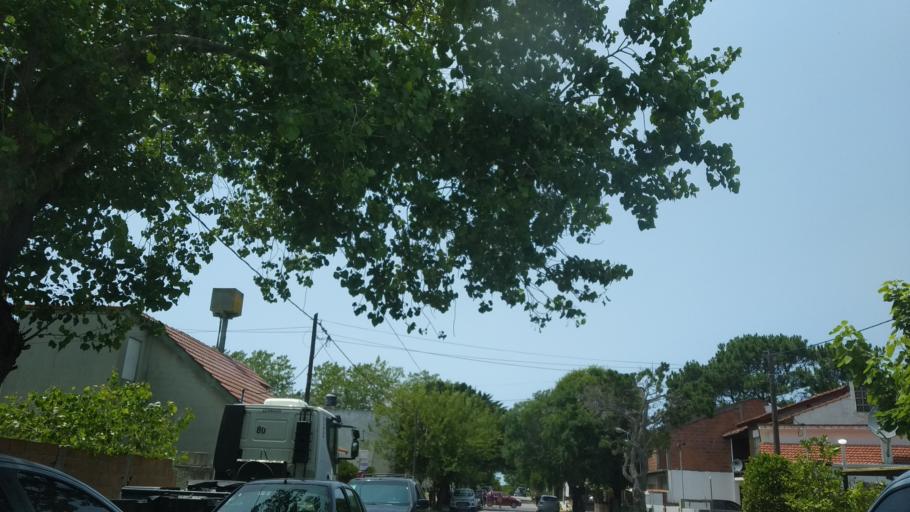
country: AR
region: Buenos Aires
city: Mar del Tuyu
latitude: -36.5569
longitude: -56.6922
